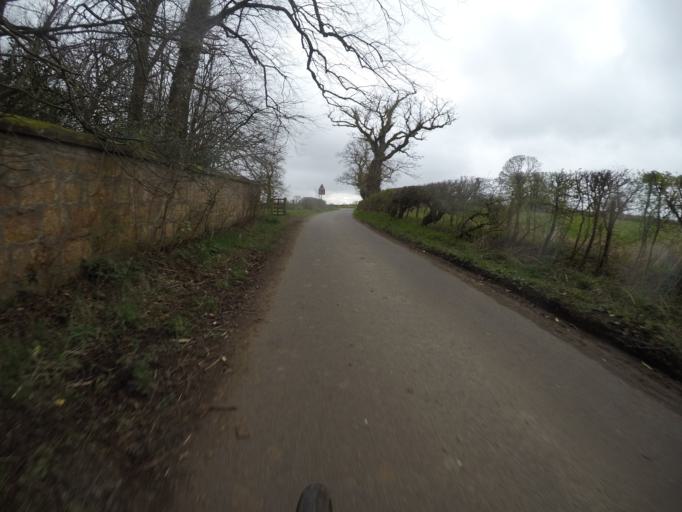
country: GB
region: Scotland
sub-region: East Ayrshire
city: Galston
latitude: 55.6070
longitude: -4.3942
